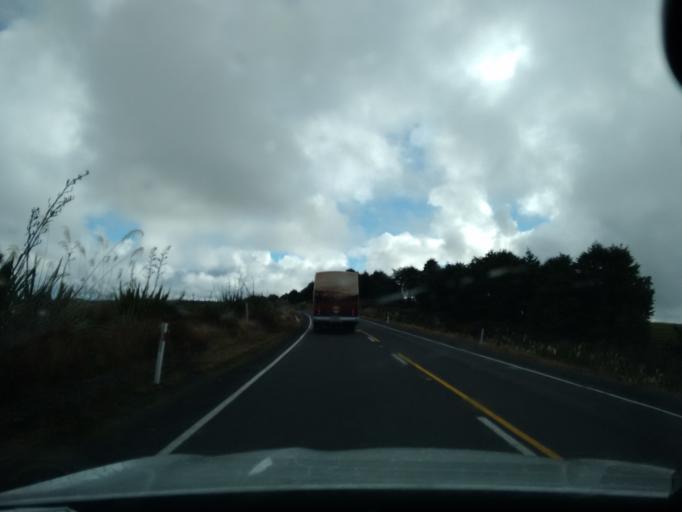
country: NZ
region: Manawatu-Wanganui
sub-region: Ruapehu District
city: Waiouru
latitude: -39.1801
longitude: 175.4492
